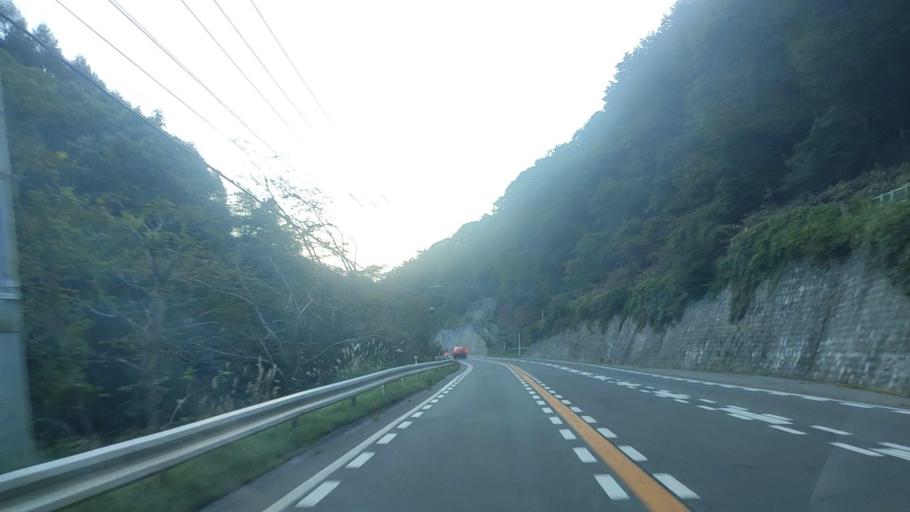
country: JP
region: Nagano
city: Suwa
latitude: 36.1269
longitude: 138.1090
